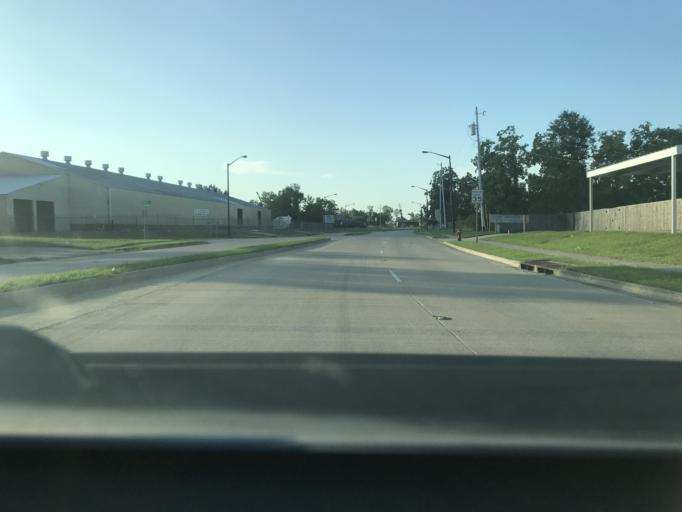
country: US
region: Louisiana
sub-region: Calcasieu Parish
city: Lake Charles
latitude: 30.2422
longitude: -93.2044
